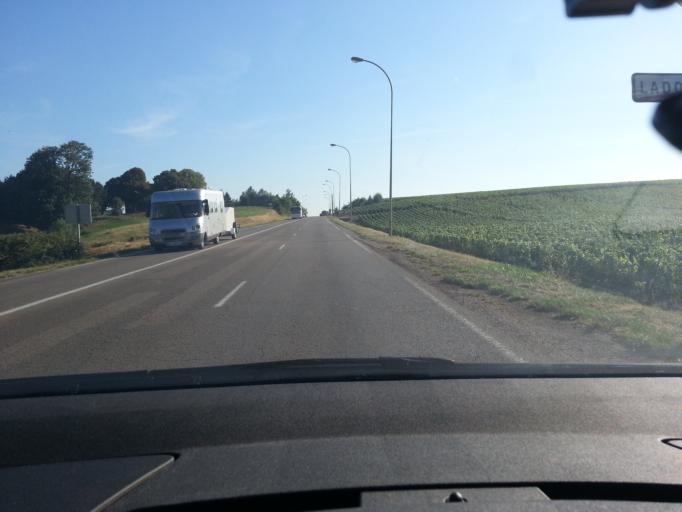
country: FR
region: Bourgogne
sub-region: Departement de la Cote-d'Or
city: Beaune
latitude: 47.0700
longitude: 4.8729
